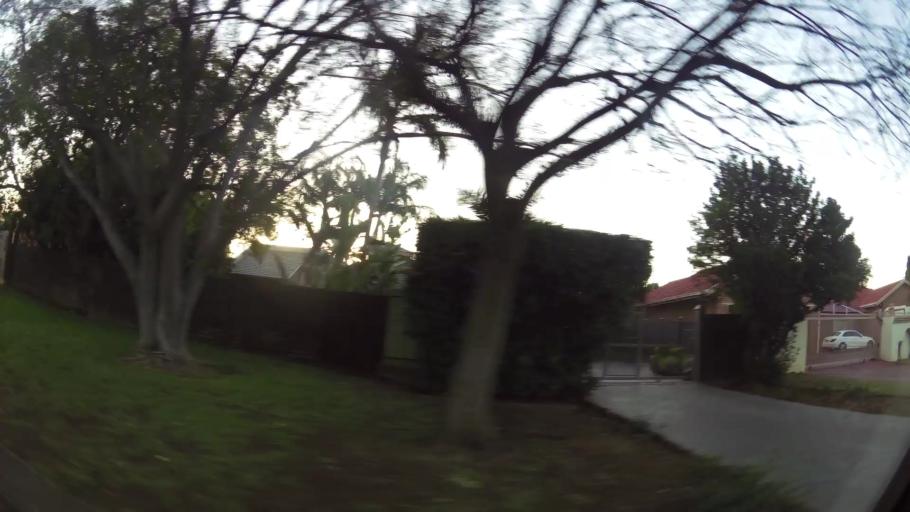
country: ZA
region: North-West
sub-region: Bojanala Platinum District Municipality
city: Rustenburg
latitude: -25.6641
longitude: 27.2164
